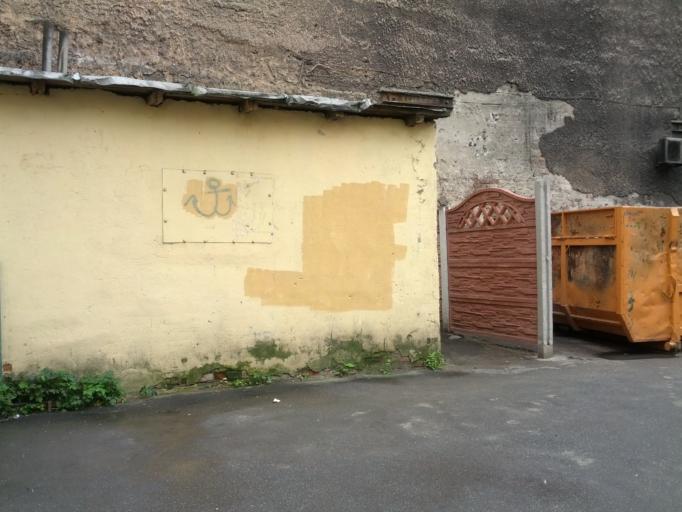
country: RU
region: St.-Petersburg
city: Saint Petersburg
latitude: 59.9163
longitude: 30.3212
